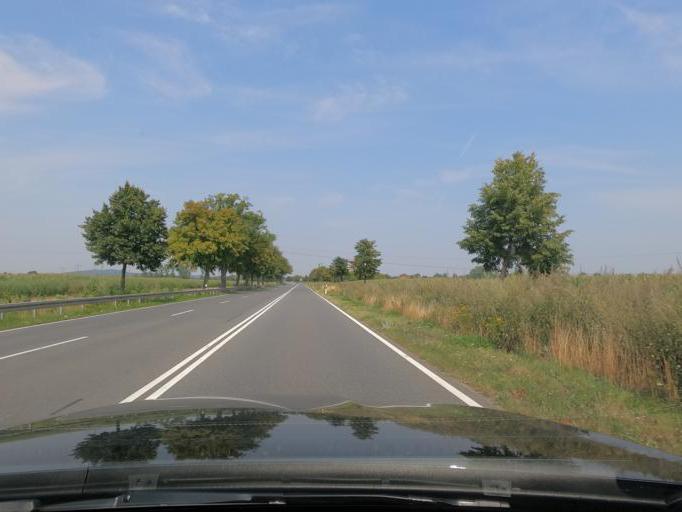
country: DE
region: Lower Saxony
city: Gehrden
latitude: 52.2850
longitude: 9.6289
